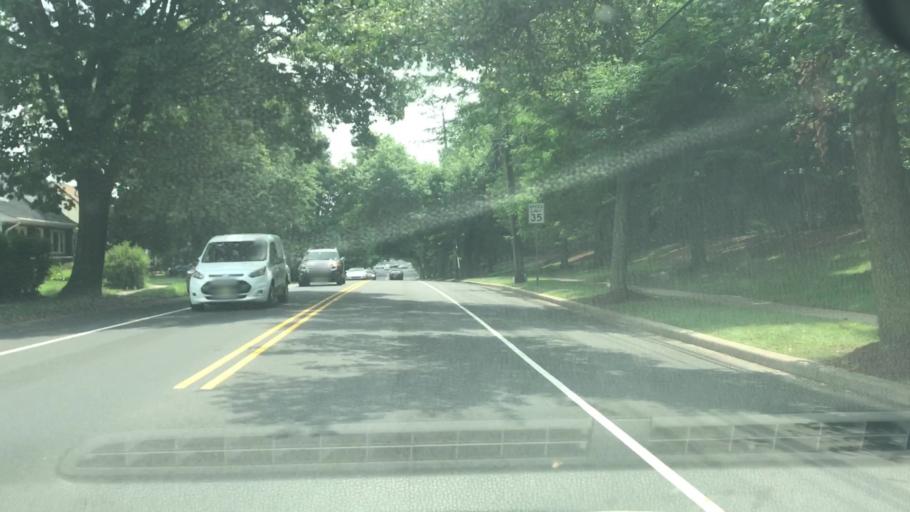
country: US
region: New Jersey
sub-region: Union County
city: Clark
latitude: 40.6377
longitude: -74.3048
